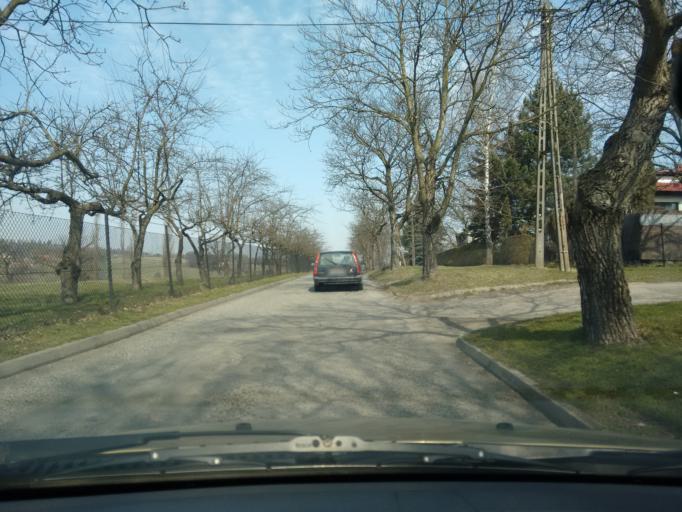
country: PL
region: Silesian Voivodeship
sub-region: Powiat cieszynski
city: Zamarski
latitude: 49.7506
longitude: 18.6668
